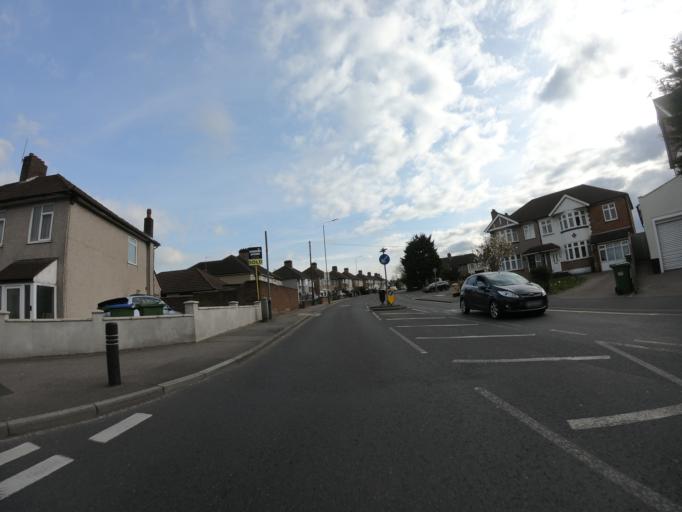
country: GB
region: England
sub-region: Greater London
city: Belvedere
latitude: 51.4772
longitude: 0.1453
